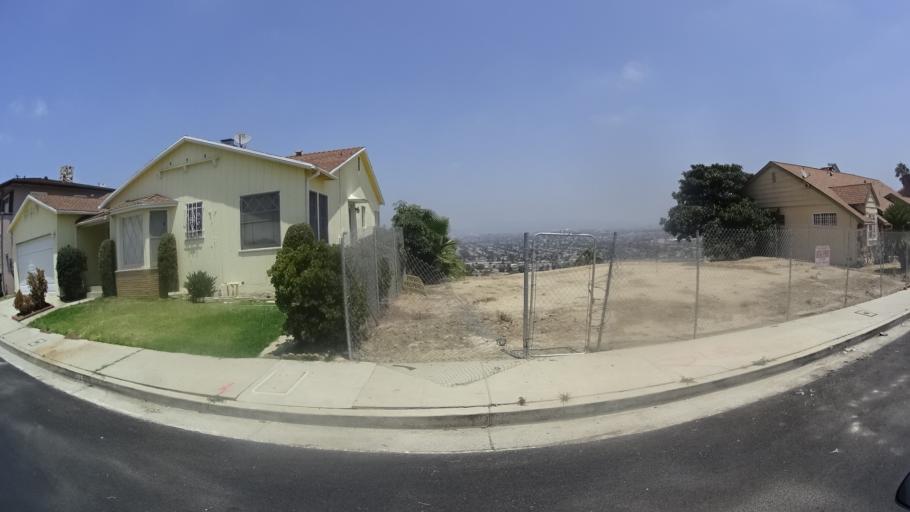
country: US
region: California
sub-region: Los Angeles County
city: View Park-Windsor Hills
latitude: 34.0063
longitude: -118.3449
